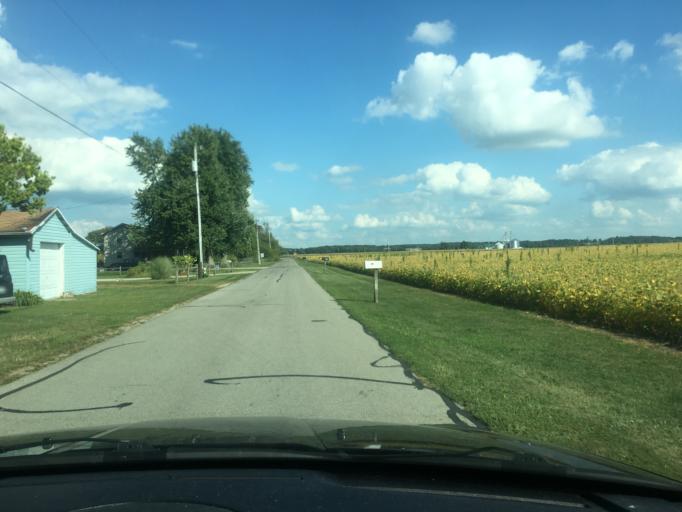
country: US
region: Ohio
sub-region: Logan County
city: West Liberty
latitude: 40.2482
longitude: -83.7505
